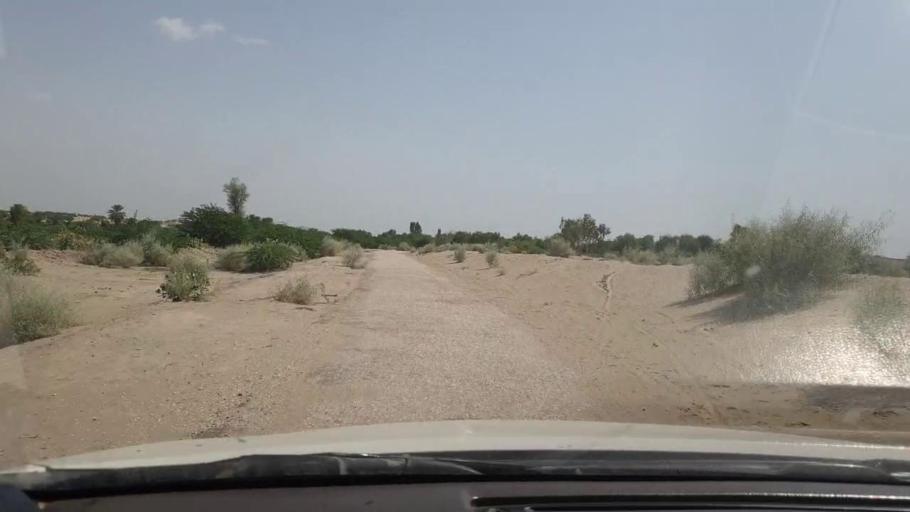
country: PK
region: Sindh
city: Rohri
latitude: 27.4662
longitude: 69.0789
